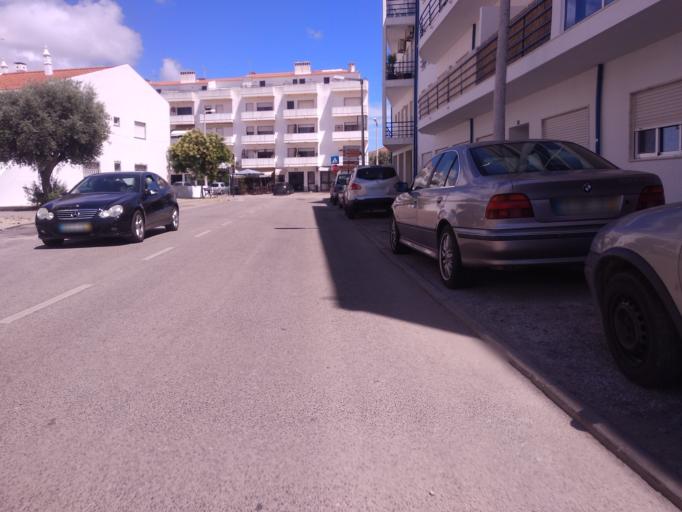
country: PT
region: Faro
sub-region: Sao Bras de Alportel
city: Sao Bras de Alportel
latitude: 37.1559
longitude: -7.8866
